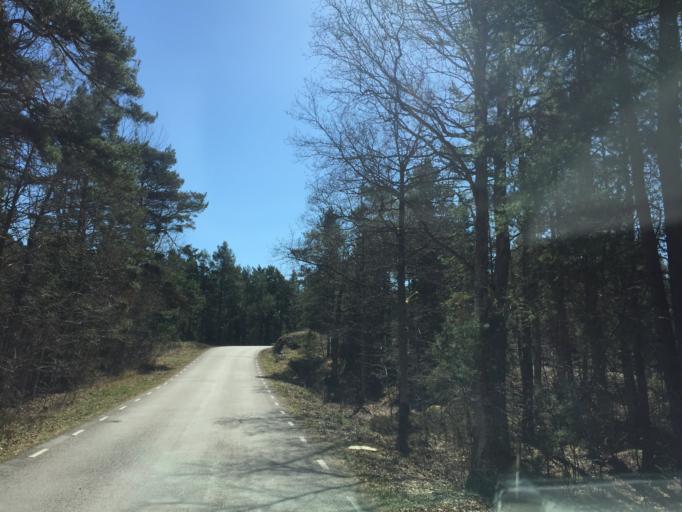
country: SE
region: Kalmar
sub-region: Oskarshamns Kommun
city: Oskarshamn
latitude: 57.2374
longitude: 16.4786
